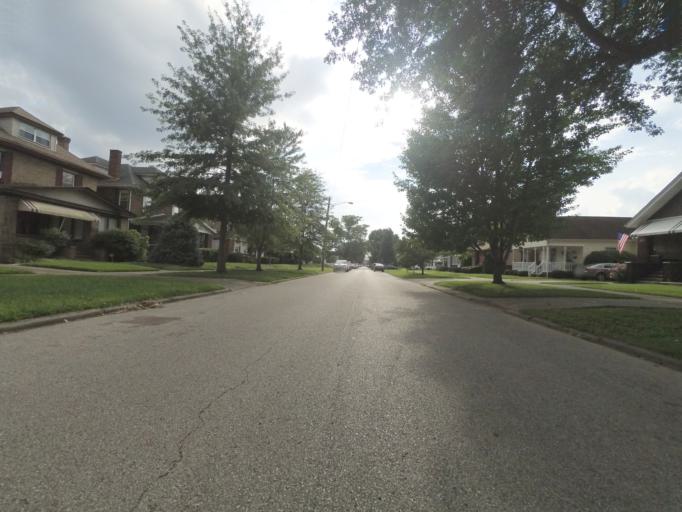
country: US
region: West Virginia
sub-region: Cabell County
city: Huntington
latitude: 38.4289
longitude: -82.4117
